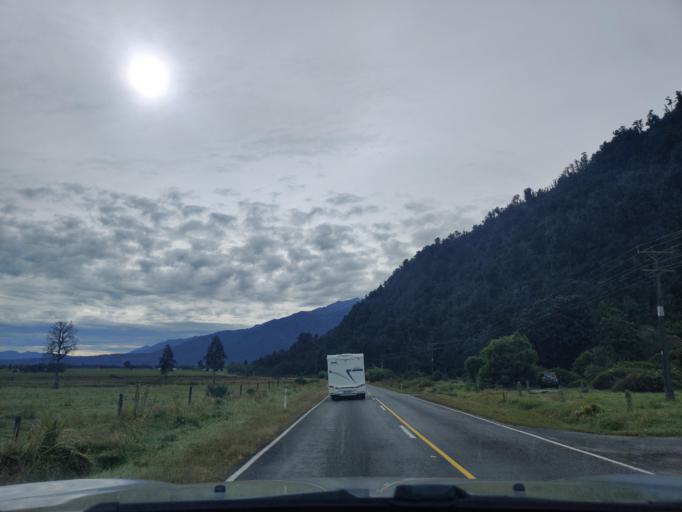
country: NZ
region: West Coast
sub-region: Westland District
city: Hokitika
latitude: -43.2798
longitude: 170.3412
